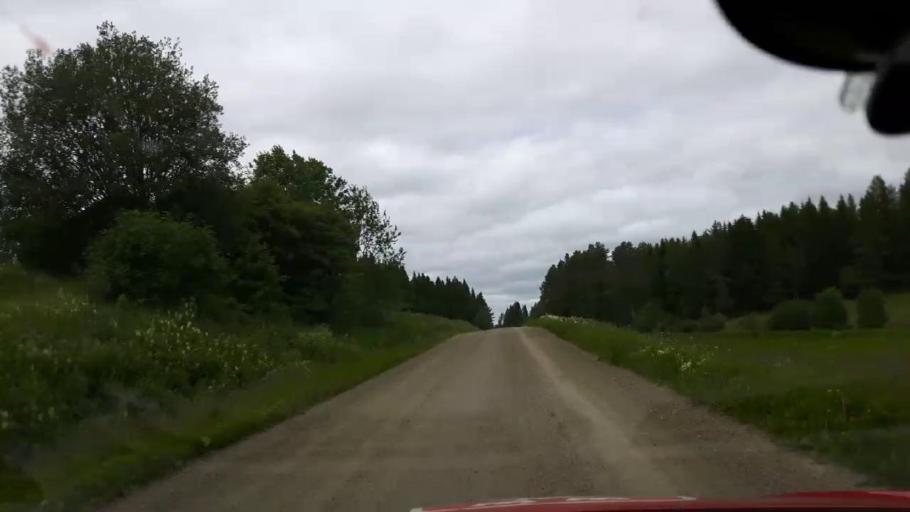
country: SE
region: Jaemtland
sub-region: OEstersunds Kommun
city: Brunflo
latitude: 62.9211
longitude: 15.0133
